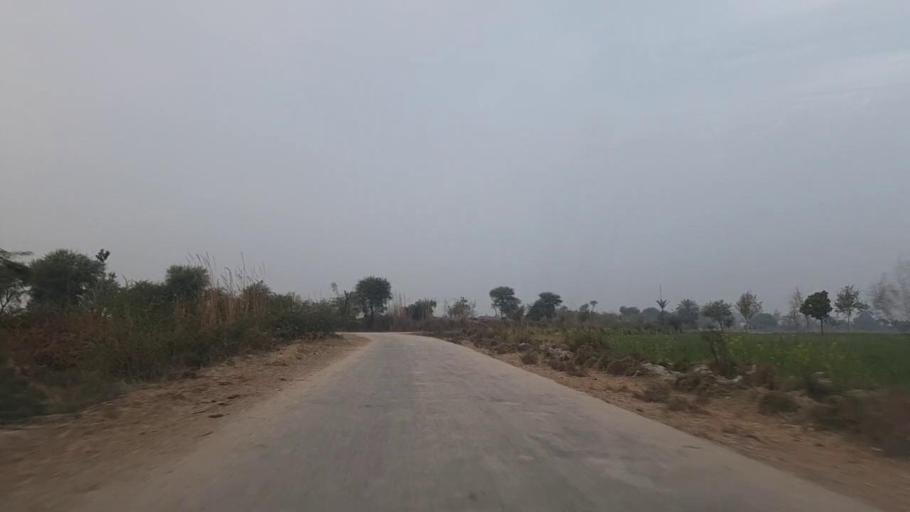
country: PK
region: Sindh
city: Jam Sahib
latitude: 26.3238
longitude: 68.5442
